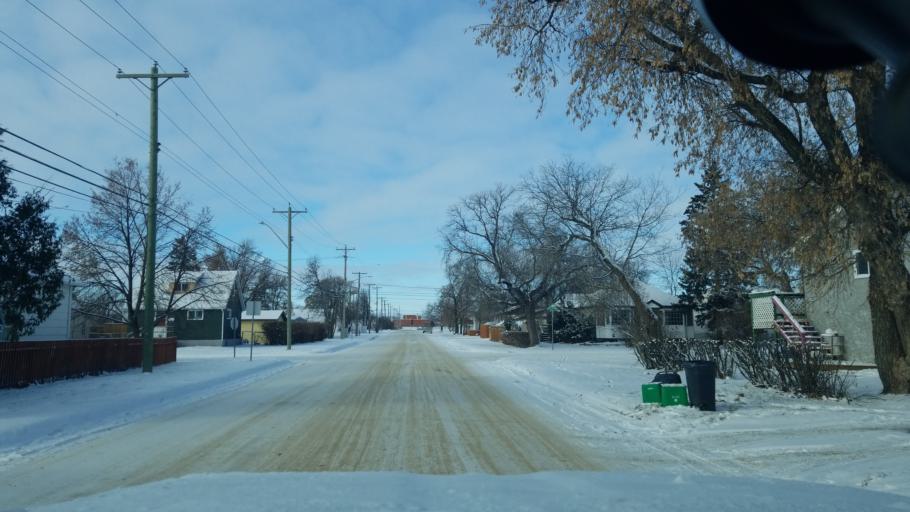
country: CA
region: Manitoba
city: Portage la Prairie
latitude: 49.9812
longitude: -98.3011
